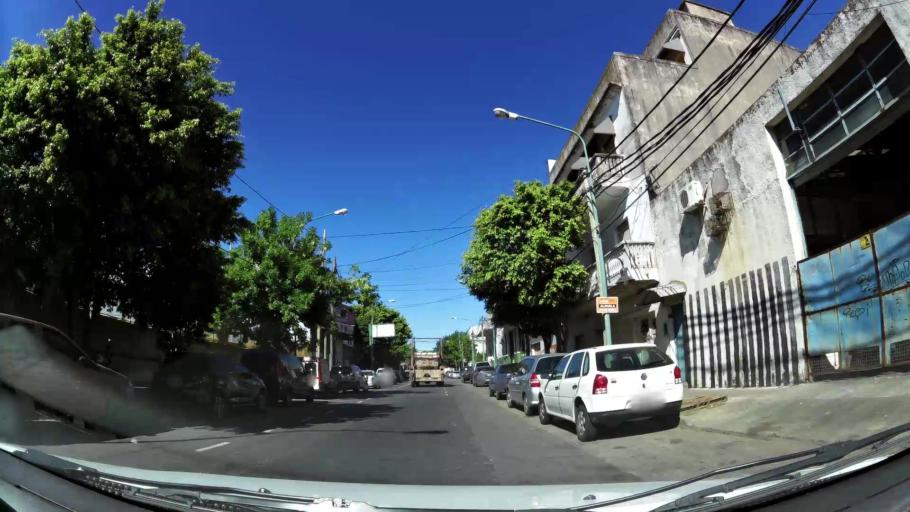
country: AR
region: Buenos Aires
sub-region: Partido de General San Martin
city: General San Martin
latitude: -34.5438
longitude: -58.5180
